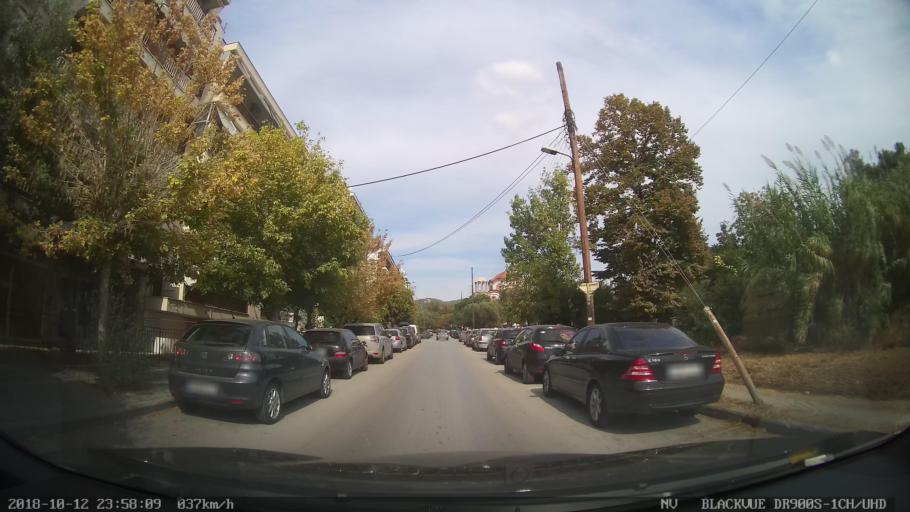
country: GR
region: Central Macedonia
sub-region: Nomos Thessalonikis
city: Pylaia
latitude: 40.6079
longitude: 22.9865
